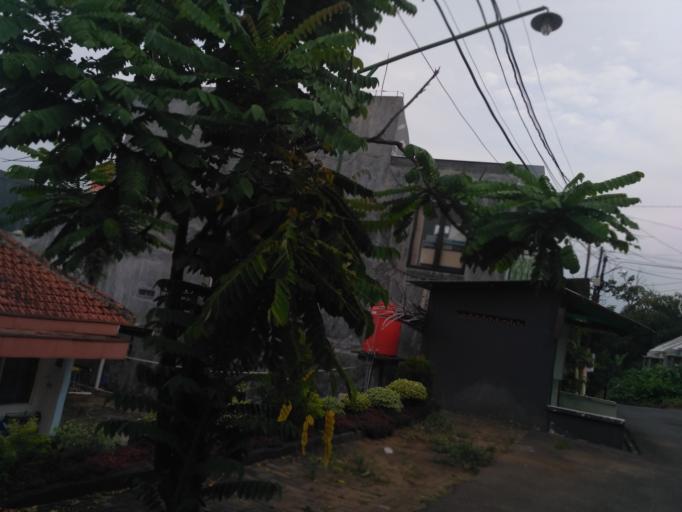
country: ID
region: Central Java
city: Ungaran
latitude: -7.0754
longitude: 110.4226
